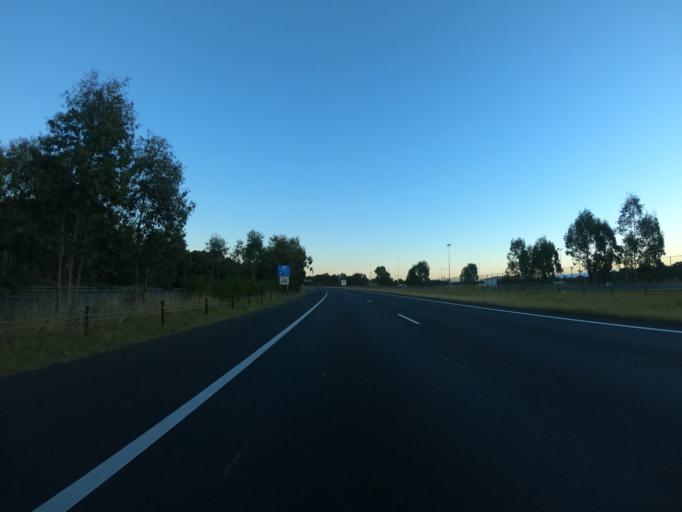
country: AU
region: New South Wales
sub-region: Blacktown
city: Doonside
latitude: -33.7774
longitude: 150.8566
